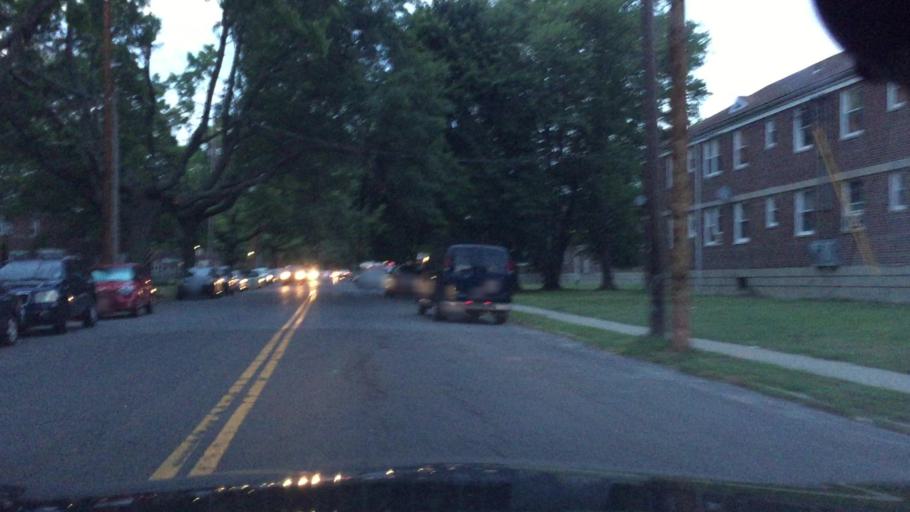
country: US
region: Connecticut
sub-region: Fairfield County
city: Stratford
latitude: 41.1986
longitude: -73.1566
